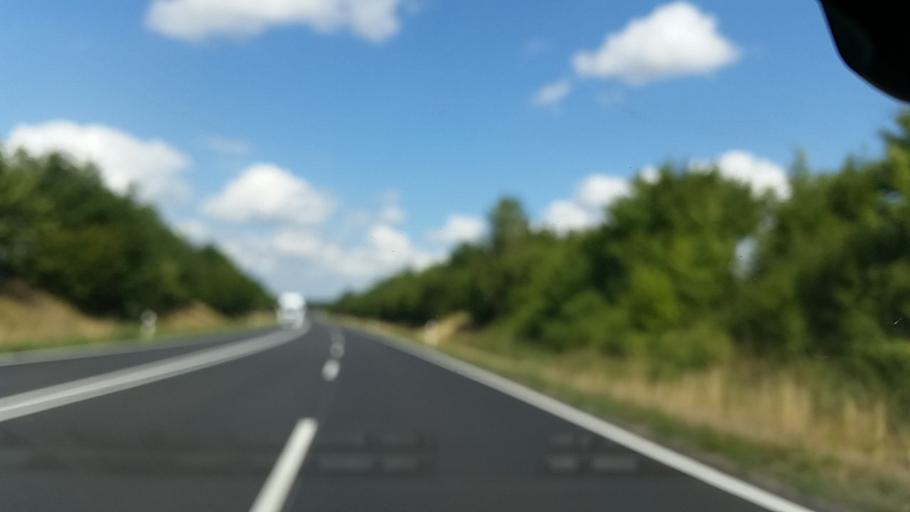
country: DE
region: Lower Saxony
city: Wrestedt
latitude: 52.9209
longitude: 10.5366
